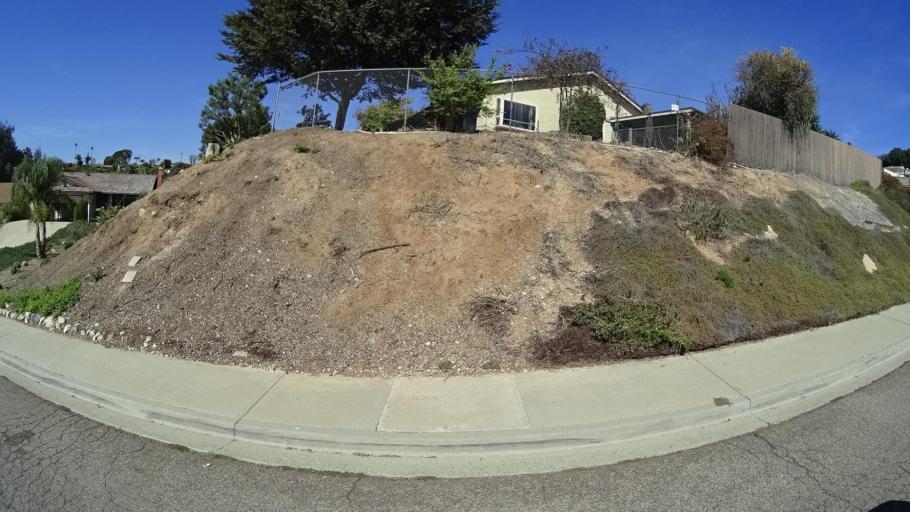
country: US
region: California
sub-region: San Diego County
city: Casa de Oro-Mount Helix
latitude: 32.7499
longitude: -116.9746
